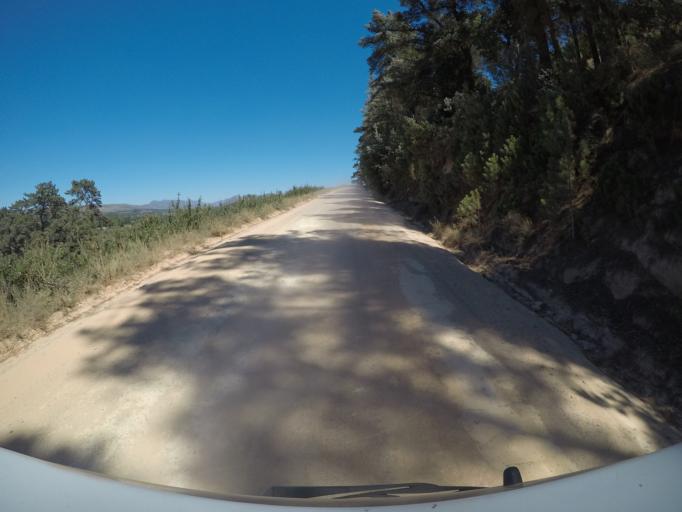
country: ZA
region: Western Cape
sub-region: Overberg District Municipality
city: Grabouw
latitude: -34.2426
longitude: 19.0892
